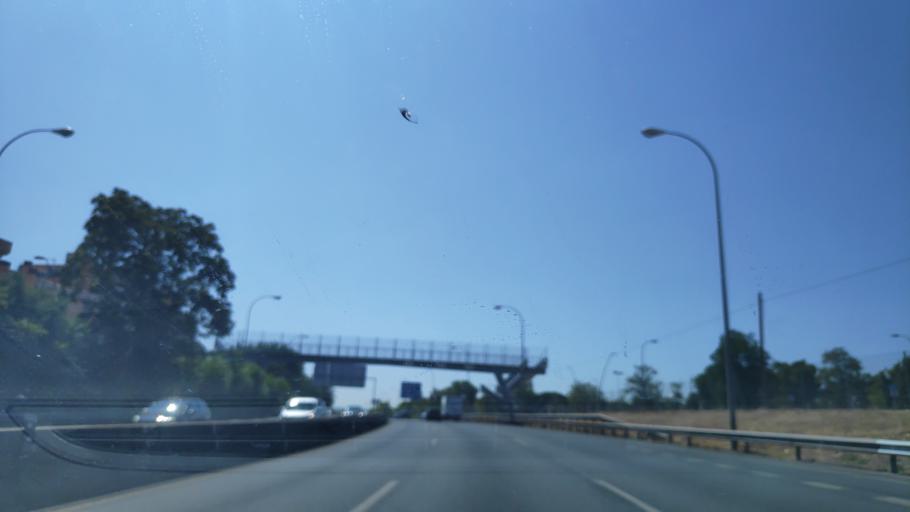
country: ES
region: Madrid
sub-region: Provincia de Madrid
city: Getafe
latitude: 40.3100
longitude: -3.7406
